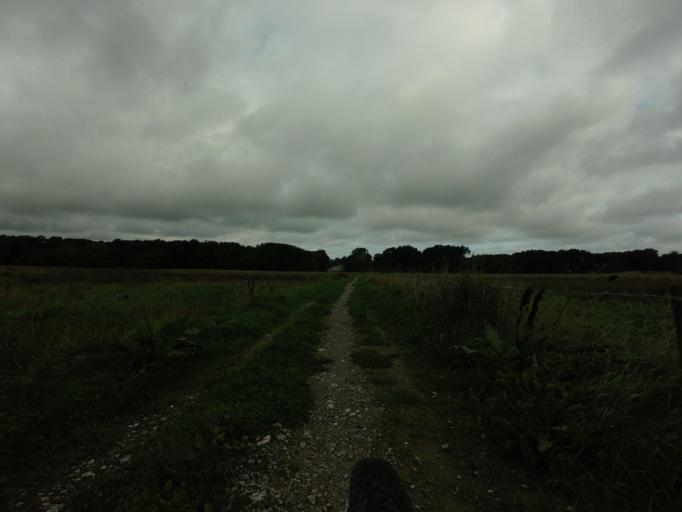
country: DK
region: North Denmark
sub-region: Hjorring Kommune
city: Hjorring
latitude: 57.4778
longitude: 9.9776
